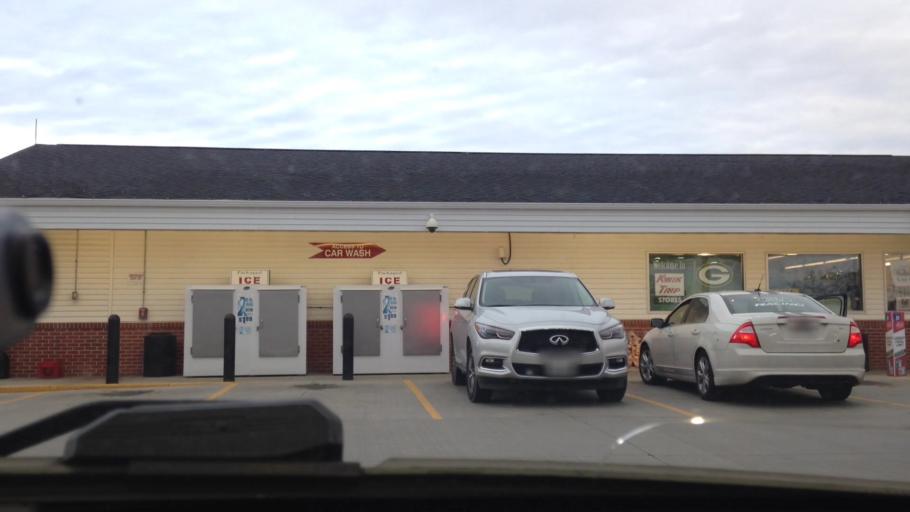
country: US
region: Wisconsin
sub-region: Fond du Lac County
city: North Fond du Lac
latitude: 43.7849
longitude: -88.4870
